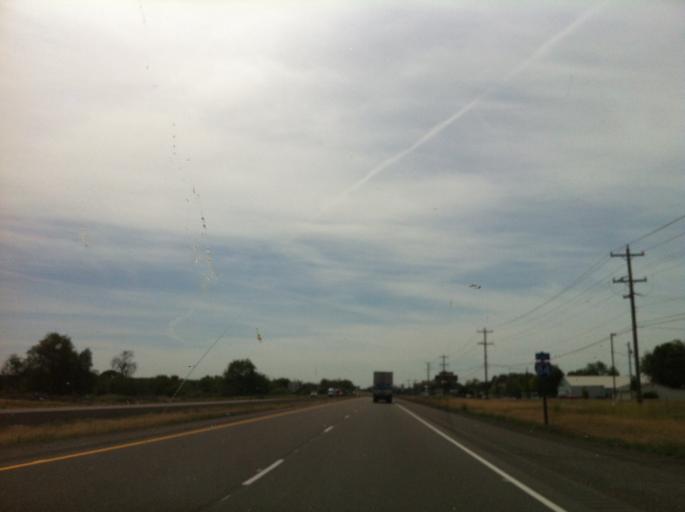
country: US
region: Oregon
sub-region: Malheur County
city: Ontario
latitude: 44.0479
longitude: -116.9755
